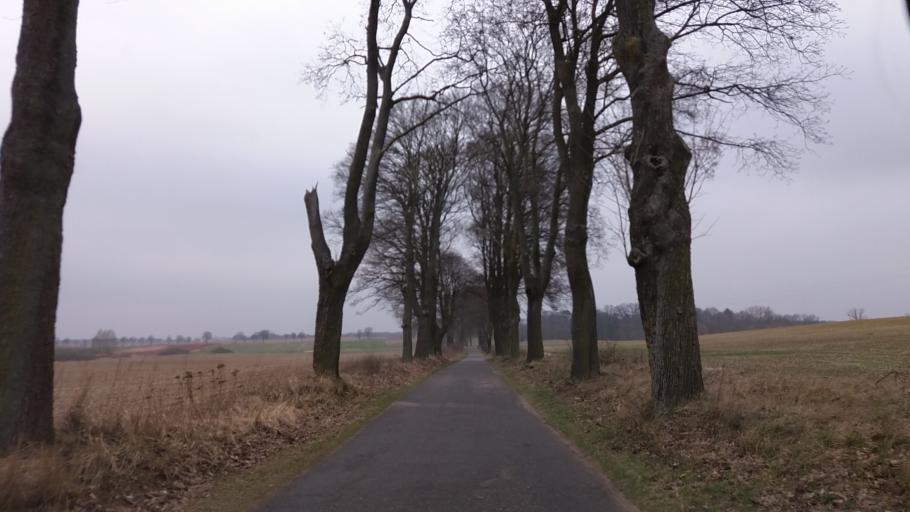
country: PL
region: West Pomeranian Voivodeship
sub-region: Powiat choszczenski
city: Choszczno
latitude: 53.1379
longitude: 15.3584
